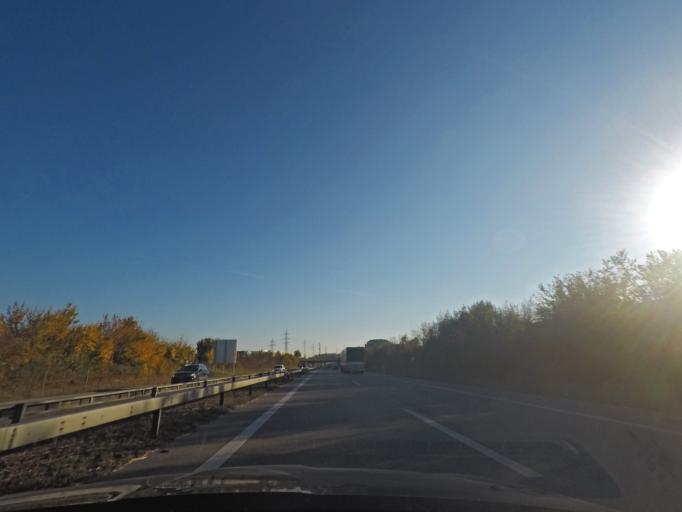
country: CH
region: Solothurn
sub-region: Bezirk Wasseramt
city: Derendingen
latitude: 47.2014
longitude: 7.6001
